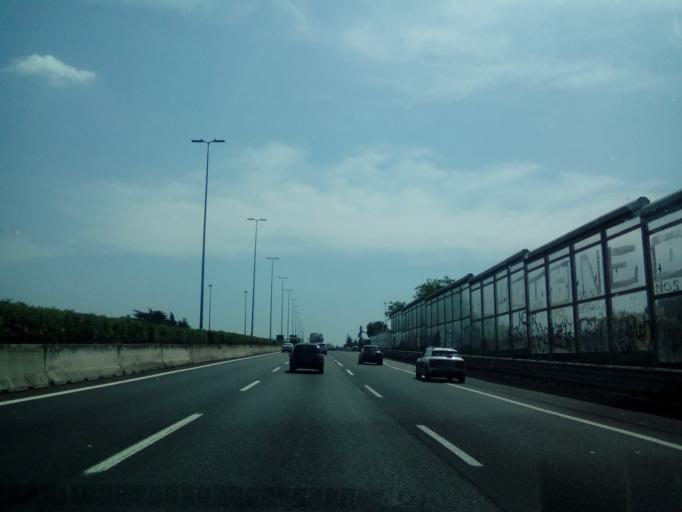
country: IT
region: Latium
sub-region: Citta metropolitana di Roma Capitale
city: Ciampino
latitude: 41.8679
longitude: 12.6029
